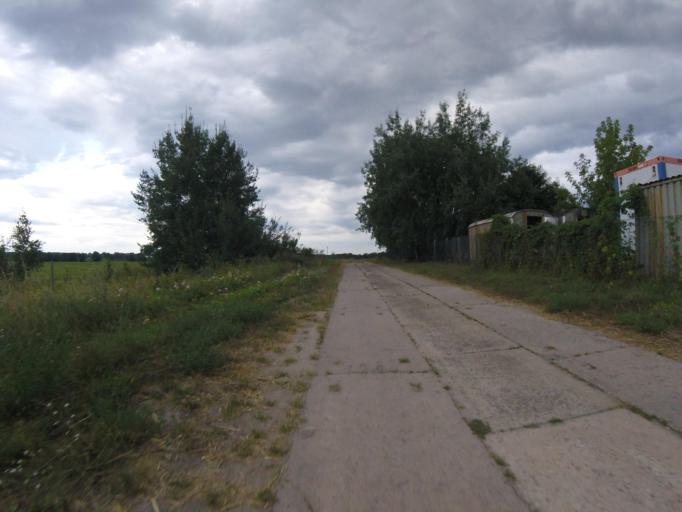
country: DE
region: Brandenburg
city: Mittenwalde
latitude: 52.2788
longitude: 13.5147
